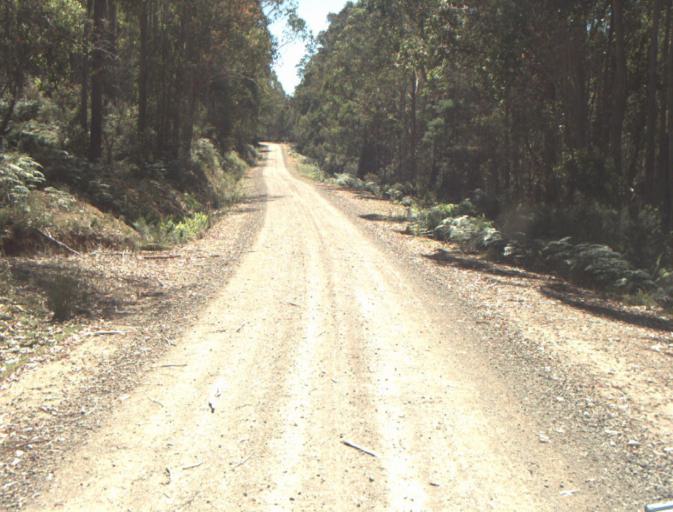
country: AU
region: Tasmania
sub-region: Dorset
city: Scottsdale
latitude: -41.3802
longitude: 147.4947
